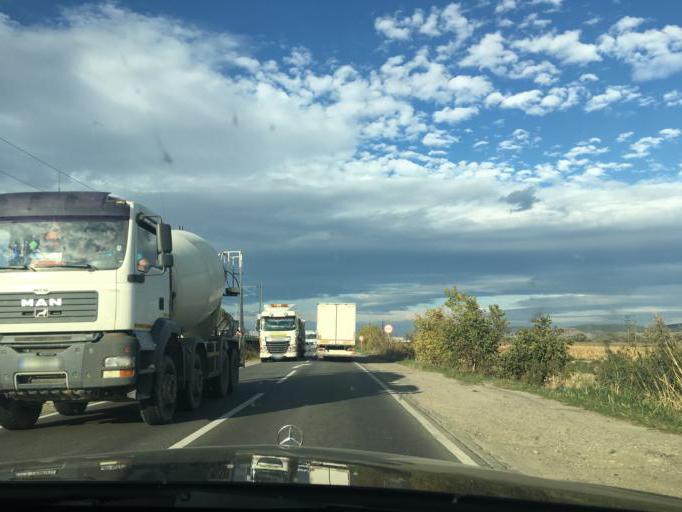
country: RO
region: Alba
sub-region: Municipiul Alba Iulia
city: Alba Iulia
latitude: 46.0658
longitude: 23.5912
